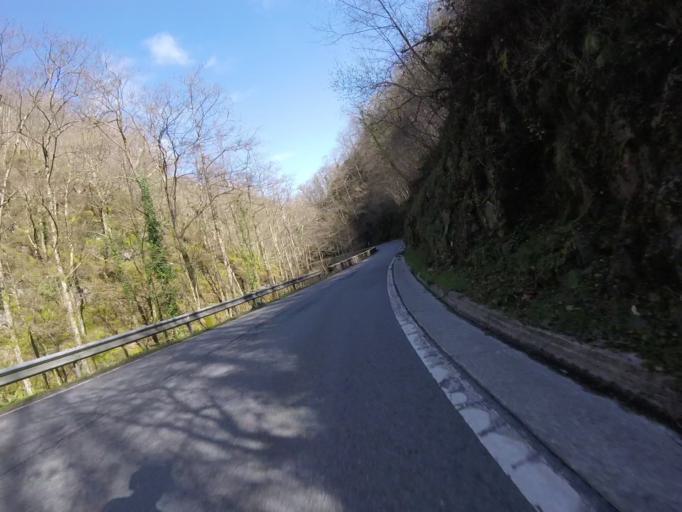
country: ES
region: Navarre
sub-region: Provincia de Navarra
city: Ezkurra
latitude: 43.1143
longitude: -1.8540
